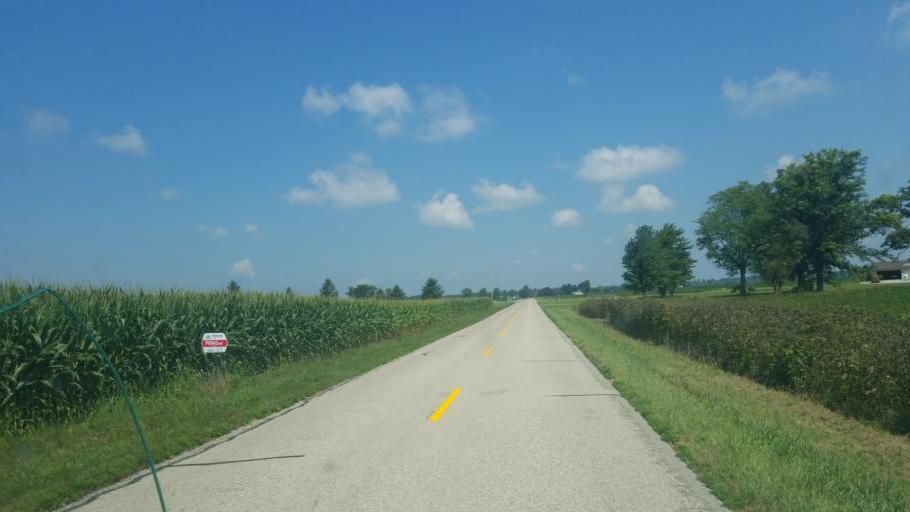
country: US
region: Ohio
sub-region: Hardin County
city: Ada
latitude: 40.6910
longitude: -83.9123
